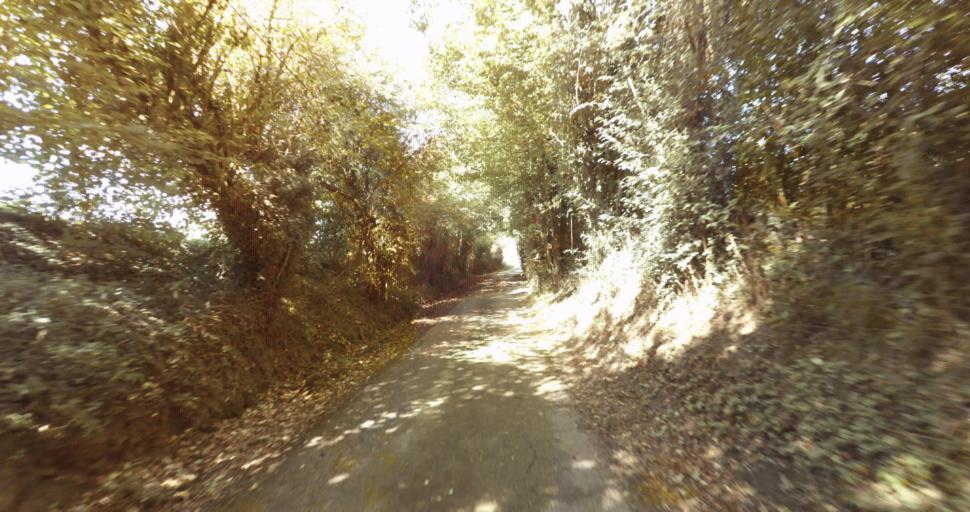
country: FR
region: Lower Normandy
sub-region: Departement de l'Orne
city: Gace
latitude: 48.7728
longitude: 0.2978
